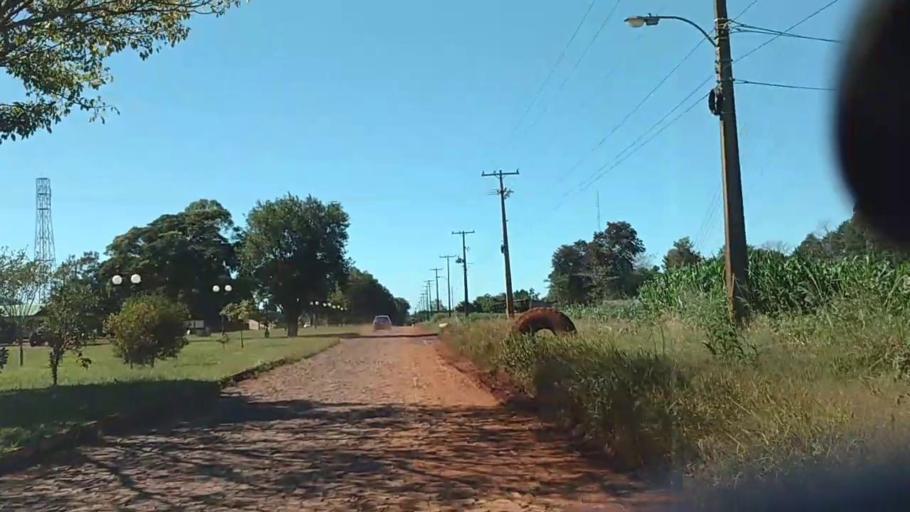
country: PY
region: Alto Parana
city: Naranjal
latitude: -25.9723
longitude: -55.1983
